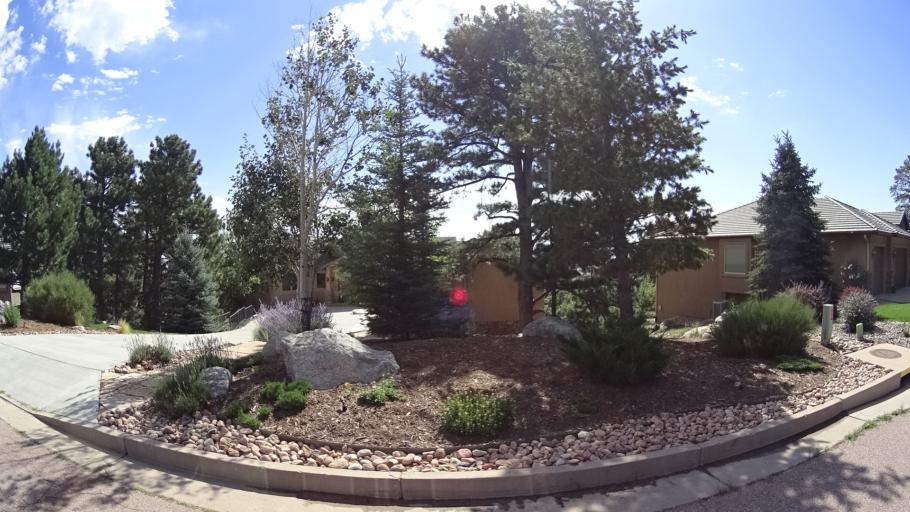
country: US
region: Colorado
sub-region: El Paso County
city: Fort Carson
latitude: 38.7462
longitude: -104.8373
